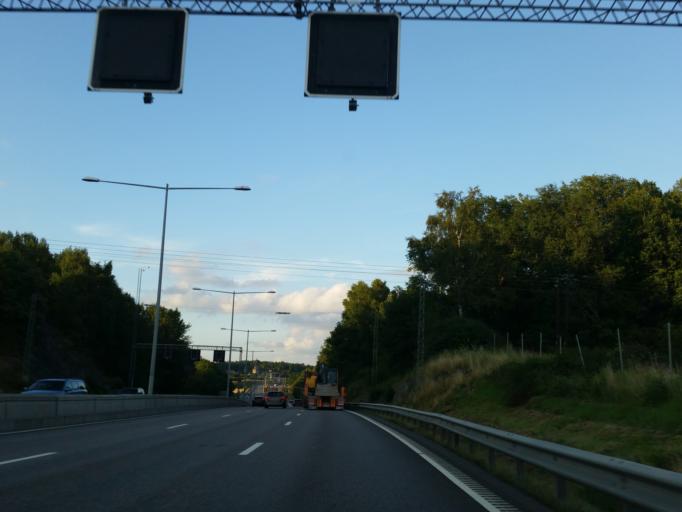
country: SE
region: Stockholm
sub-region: Botkyrka Kommun
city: Eriksberg
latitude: 59.2314
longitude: 17.8037
